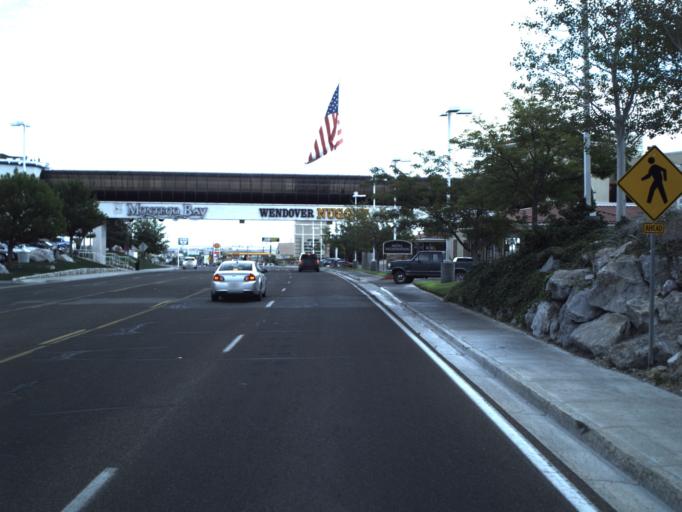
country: US
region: Utah
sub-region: Tooele County
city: Wendover
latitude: 40.7356
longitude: -114.0459
